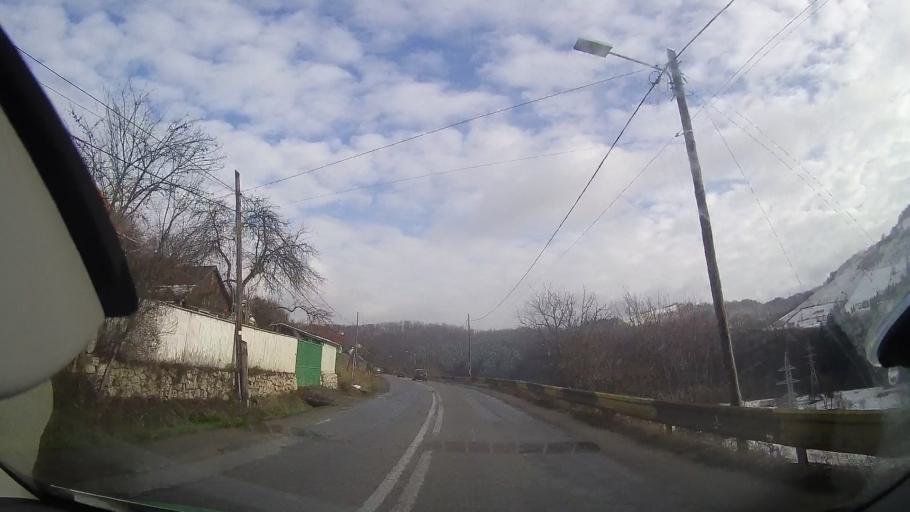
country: RO
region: Alba
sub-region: Oras Baia de Aries
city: Baia de Aries
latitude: 46.3746
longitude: 23.2566
